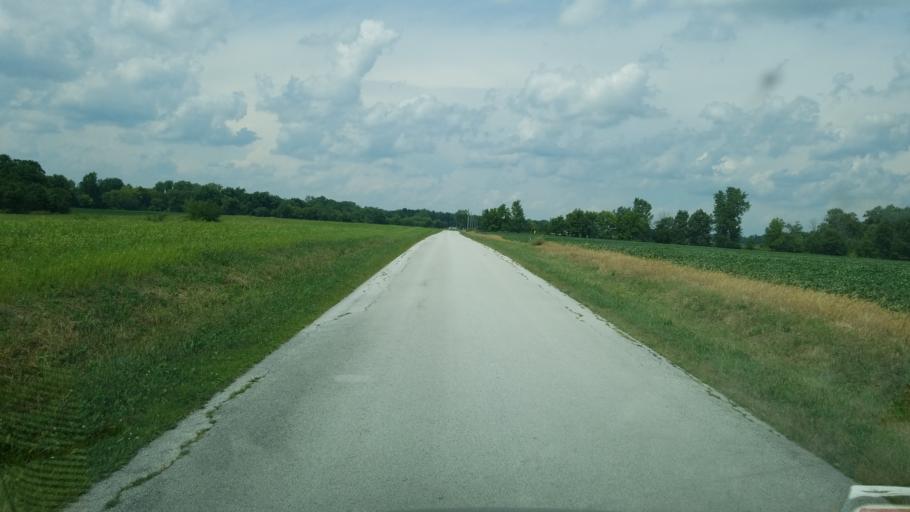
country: US
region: Ohio
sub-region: Hancock County
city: Arlington
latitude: 40.9317
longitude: -83.5430
